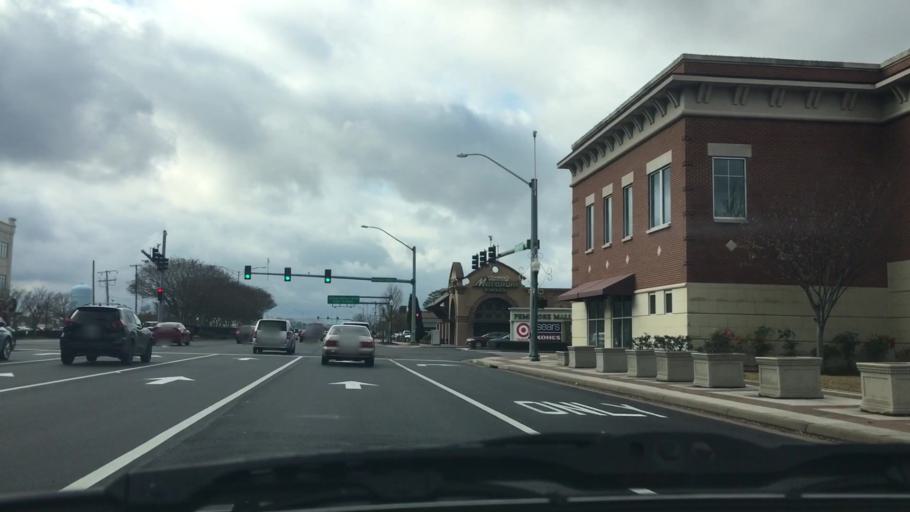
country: US
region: Virginia
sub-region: City of Chesapeake
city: Chesapeake
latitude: 36.8437
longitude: -76.1332
